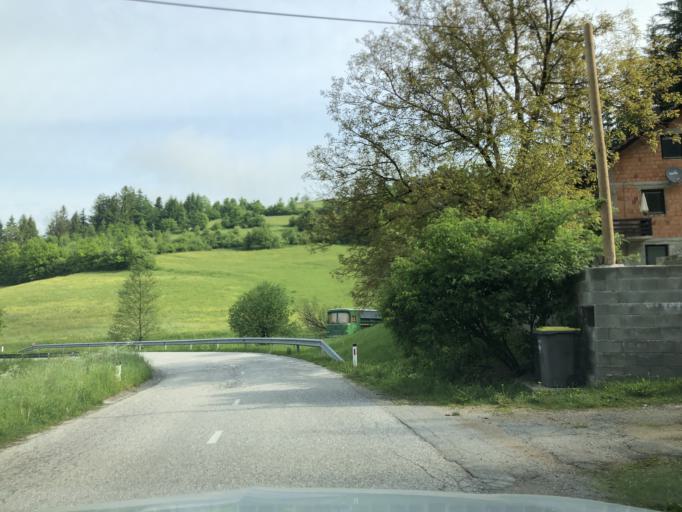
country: SI
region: Velike Lasce
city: Velike Lasce
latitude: 45.8072
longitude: 14.6150
